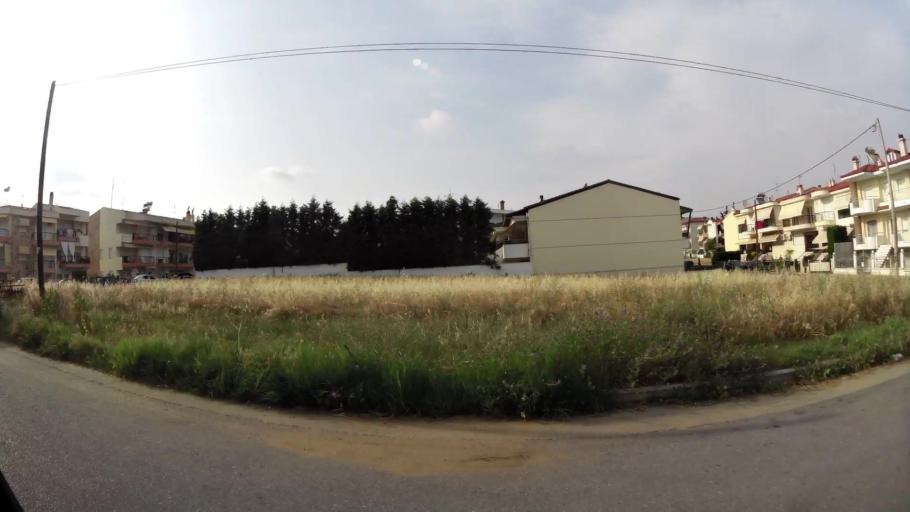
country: GR
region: Central Macedonia
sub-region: Nomos Thessalonikis
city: Oraiokastro
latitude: 40.7220
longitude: 22.9232
